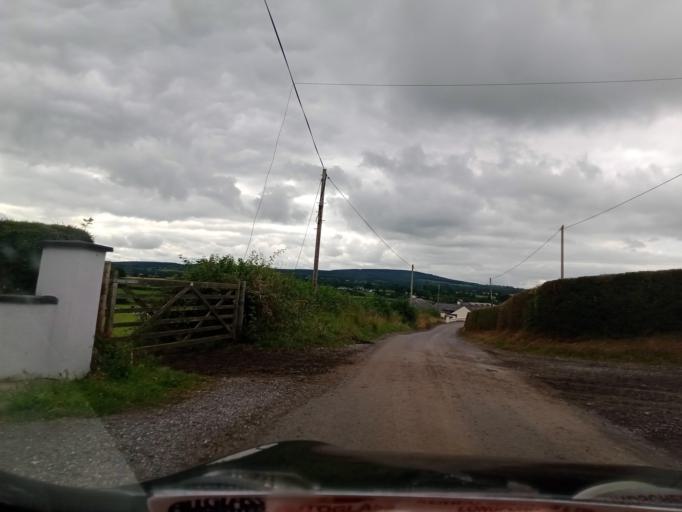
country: IE
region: Leinster
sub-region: Laois
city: Stradbally
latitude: 52.9586
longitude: -7.1915
